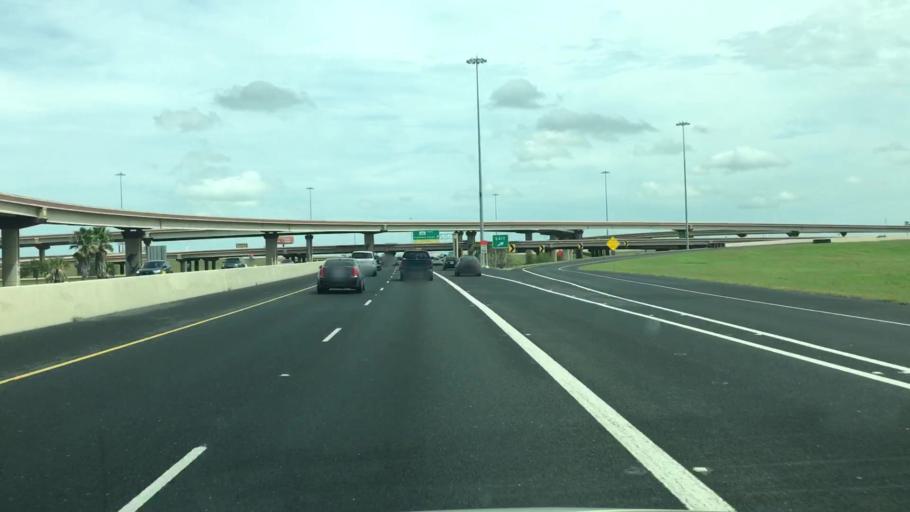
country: US
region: Texas
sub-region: Nueces County
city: Corpus Christi
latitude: 27.7386
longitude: -97.4337
